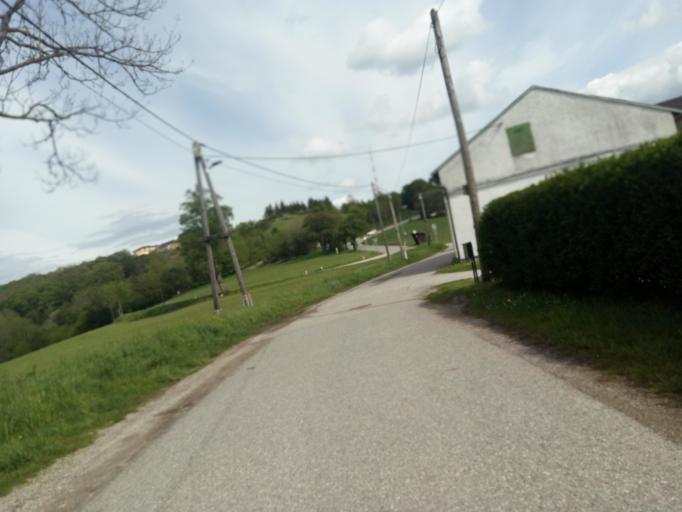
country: AT
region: Lower Austria
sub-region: Politischer Bezirk Wien-Umgebung
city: Wolfsgraben
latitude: 48.1319
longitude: 16.1070
